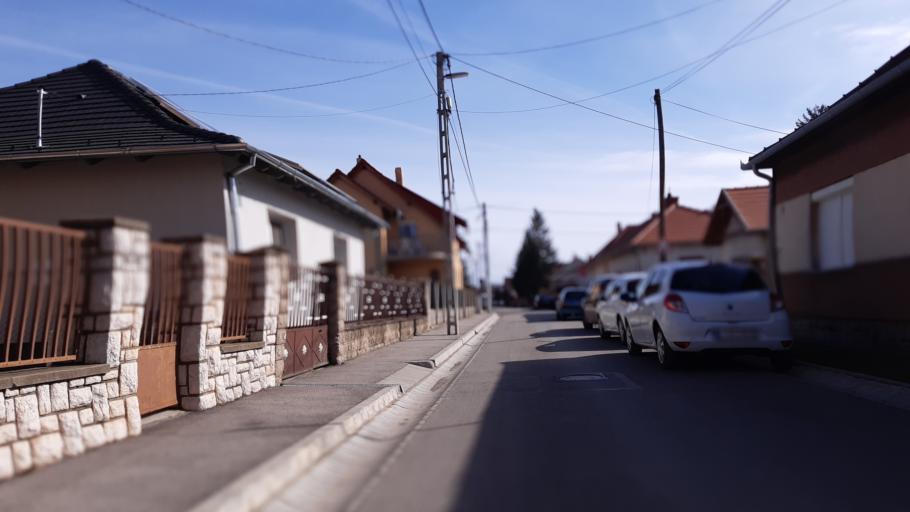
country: HU
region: Baranya
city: Pellerd
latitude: 46.0601
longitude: 18.1867
